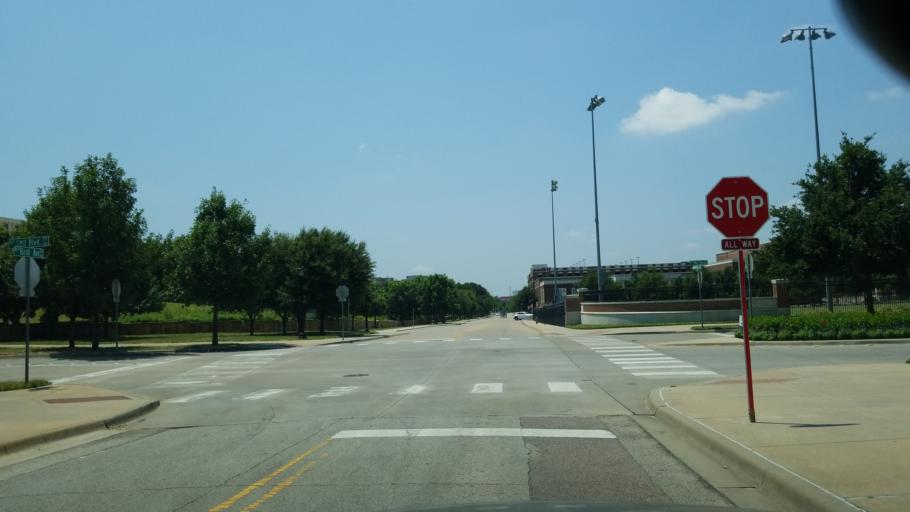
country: US
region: Texas
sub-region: Dallas County
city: Highland Park
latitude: 32.8423
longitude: -96.7794
